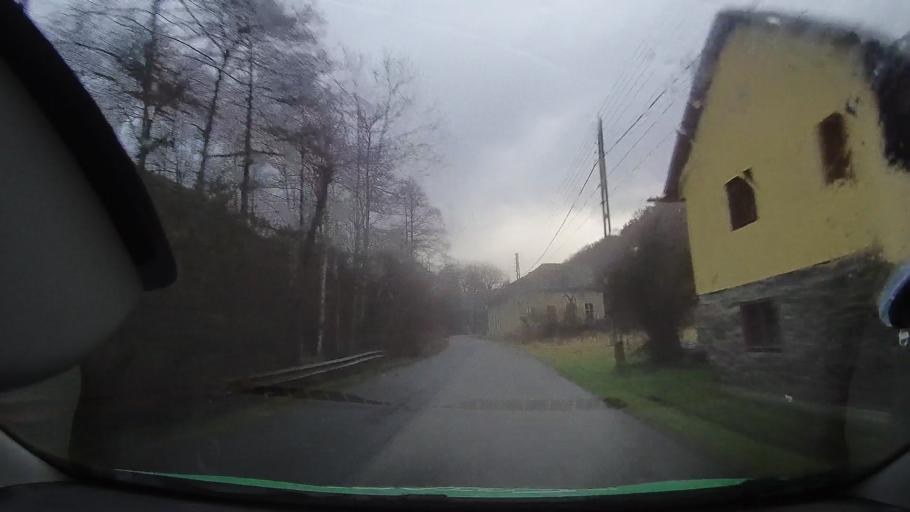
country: RO
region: Hunedoara
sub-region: Comuna Ribita
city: Ribita
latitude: 46.2613
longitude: 22.7436
